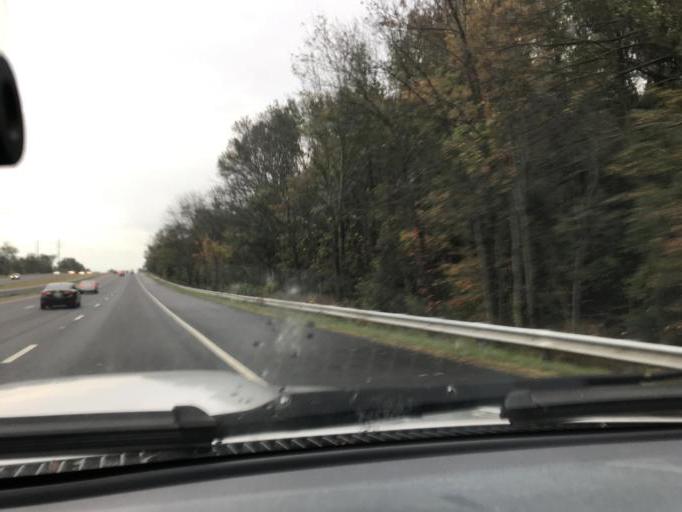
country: US
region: New Jersey
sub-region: Mercer County
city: Mercerville
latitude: 40.2682
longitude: -74.6923
